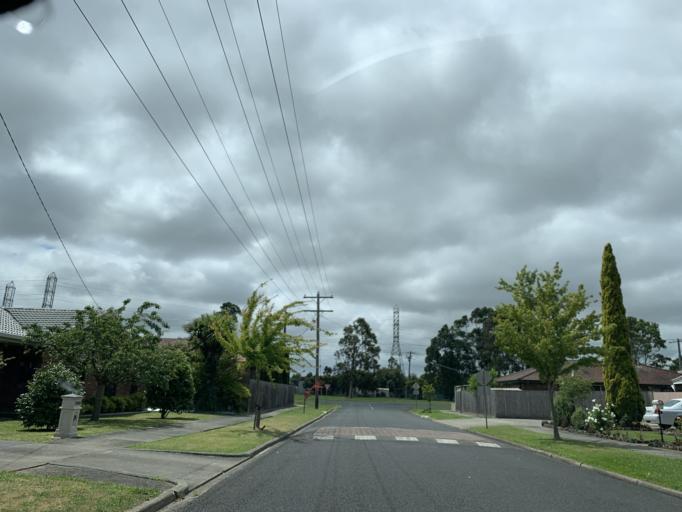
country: AU
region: Victoria
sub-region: Latrobe
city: Moe
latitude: -38.1628
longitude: 146.2656
